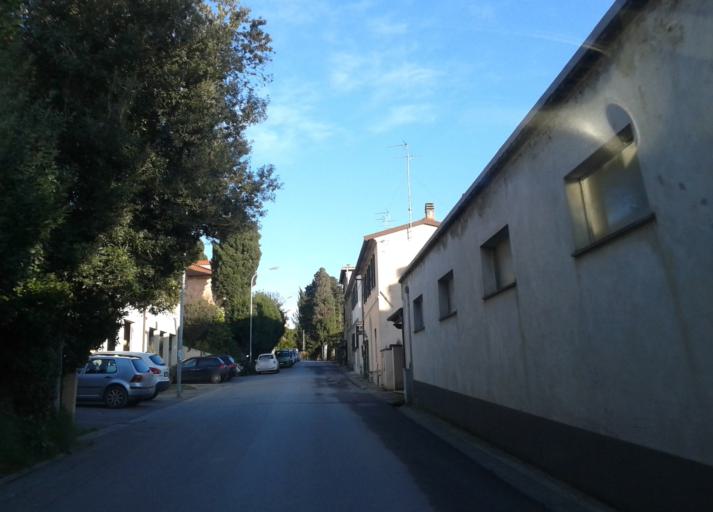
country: IT
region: Tuscany
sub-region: Provincia di Livorno
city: Guasticce
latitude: 43.5768
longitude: 10.4372
